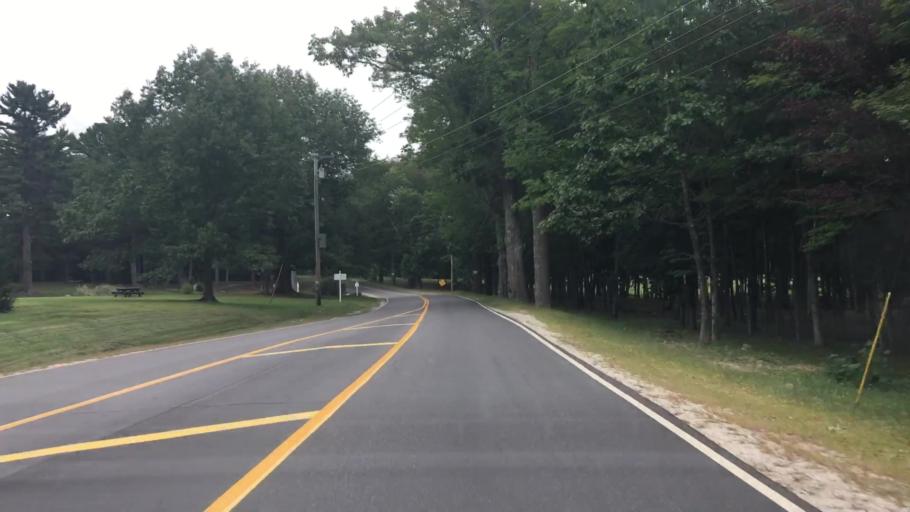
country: US
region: Maine
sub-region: Cumberland County
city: New Gloucester
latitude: 43.9014
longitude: -70.2535
